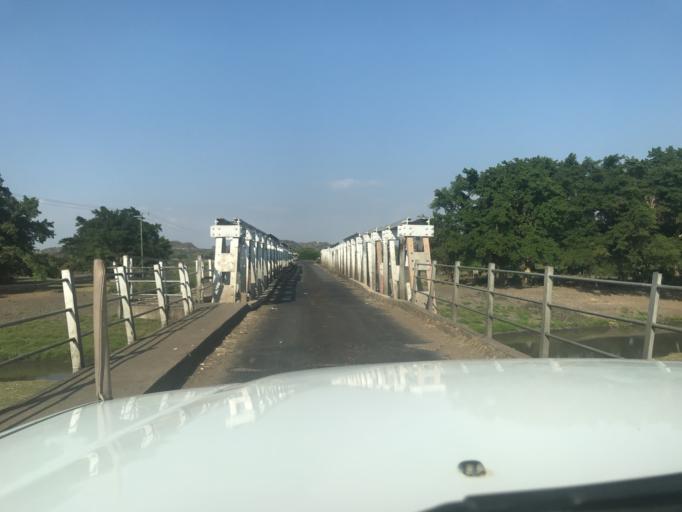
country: TZ
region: Mwanza
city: Kihangara
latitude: -2.5745
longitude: 33.4615
